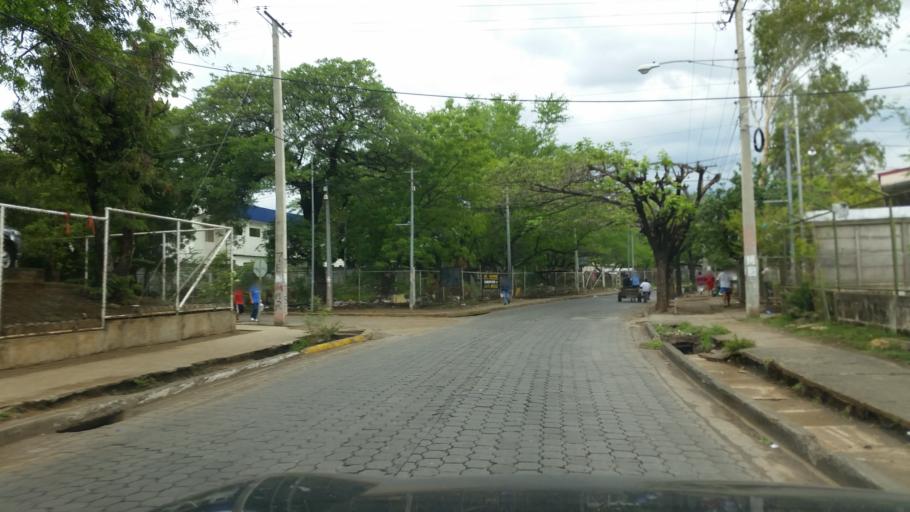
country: NI
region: Managua
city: Managua
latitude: 12.1430
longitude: -86.2617
